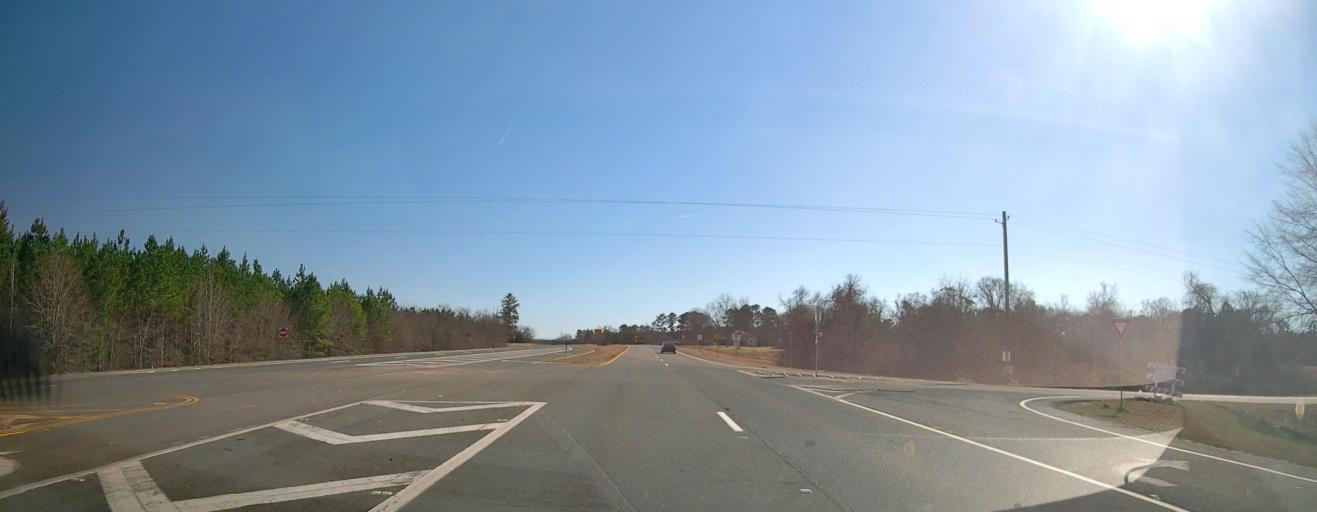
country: US
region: Georgia
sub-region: Schley County
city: Ellaville
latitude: 32.1597
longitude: -84.2703
